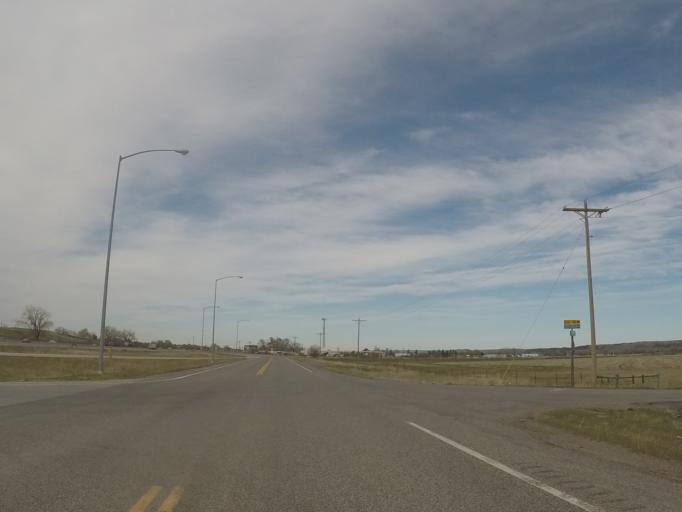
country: US
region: Montana
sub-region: Yellowstone County
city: Laurel
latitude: 45.6939
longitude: -108.6798
